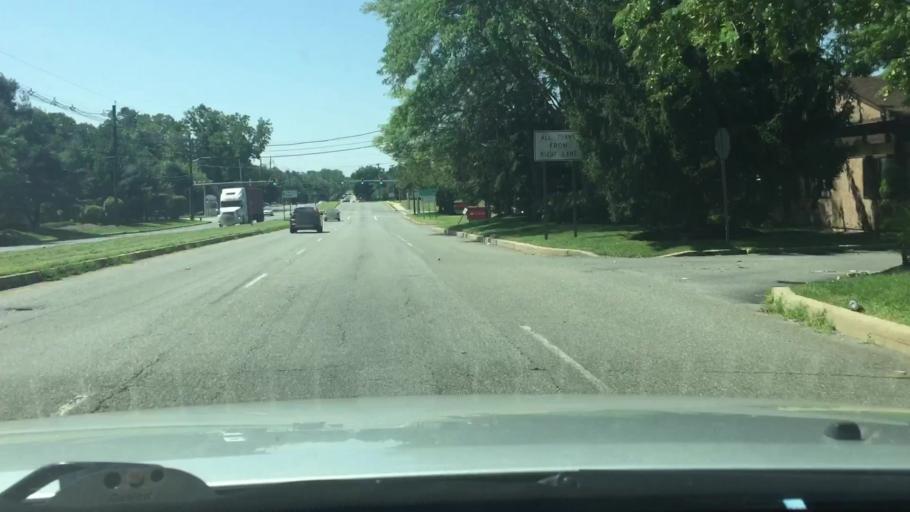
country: US
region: New Jersey
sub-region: Middlesex County
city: East Brunswick
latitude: 40.4111
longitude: -74.4188
